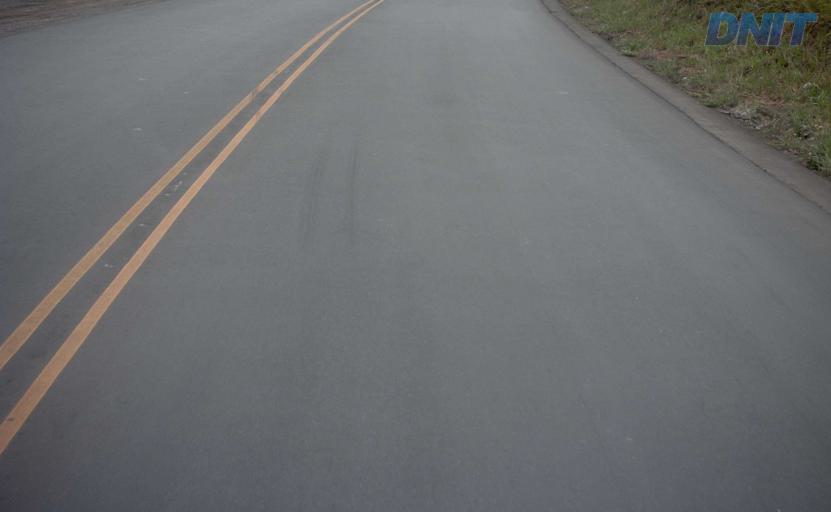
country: BR
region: Minas Gerais
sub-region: Coronel Fabriciano
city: Coronel Fabriciano
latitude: -19.5354
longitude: -42.5921
